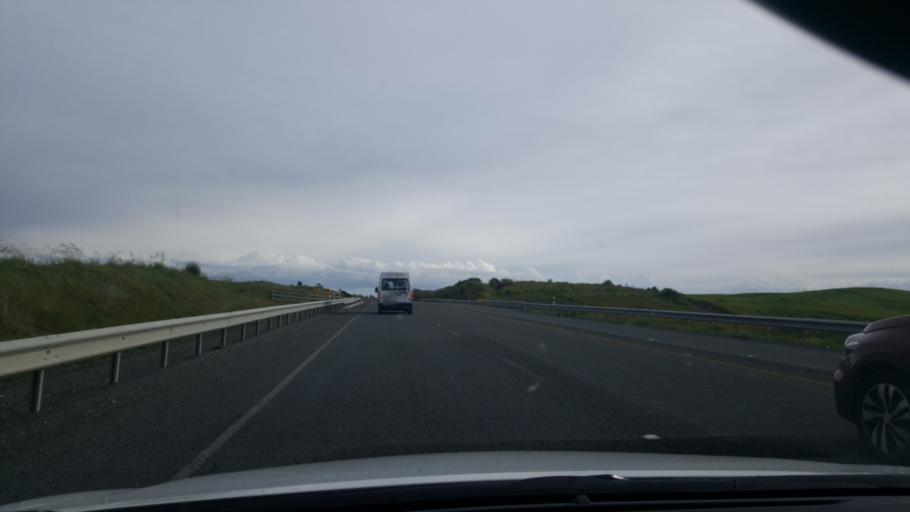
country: NZ
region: Waikato
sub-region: Taupo District
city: Taupo
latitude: -38.6446
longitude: 176.0998
